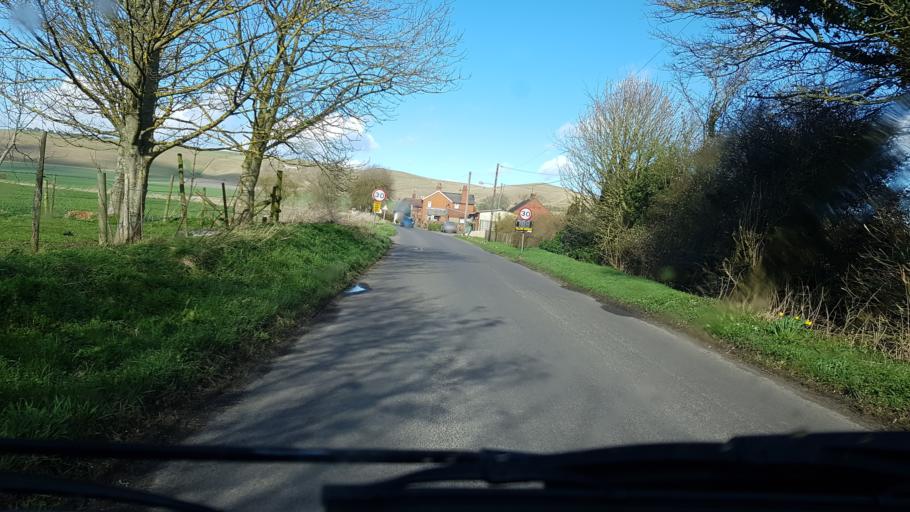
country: GB
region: England
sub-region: Wiltshire
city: Woodborough
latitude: 51.3556
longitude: -1.8511
